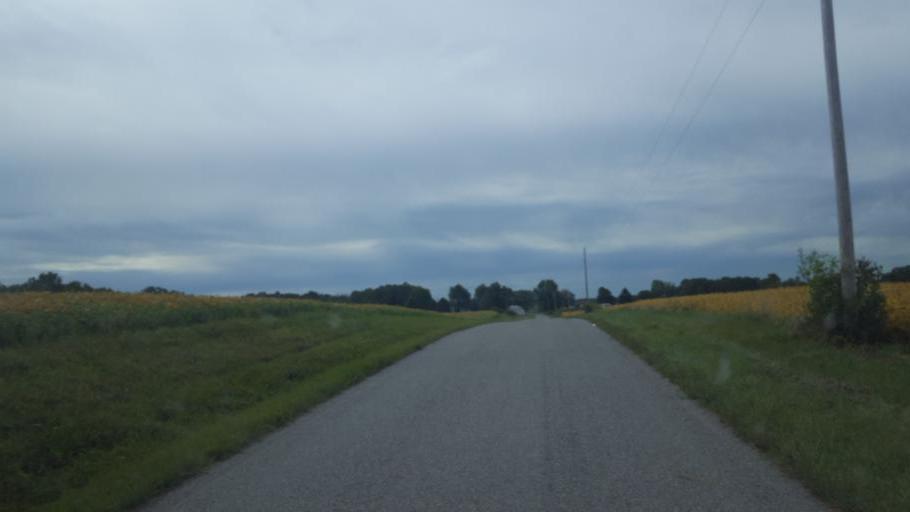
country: US
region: Ohio
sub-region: Knox County
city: Centerburg
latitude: 40.3775
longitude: -82.7364
